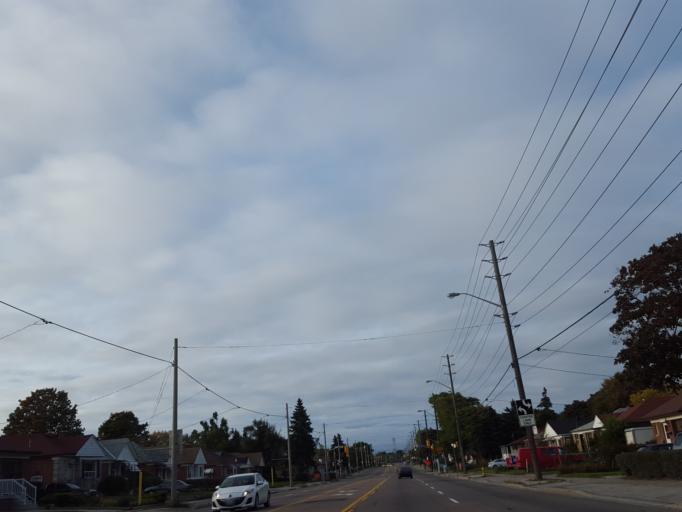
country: CA
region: Ontario
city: Scarborough
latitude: 43.7506
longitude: -79.2968
